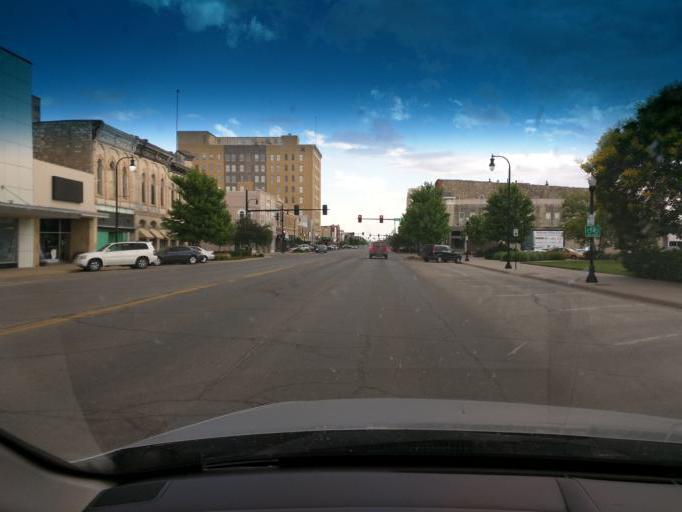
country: US
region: Kansas
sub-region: Reno County
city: Hutchinson
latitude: 38.0556
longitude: -97.9318
